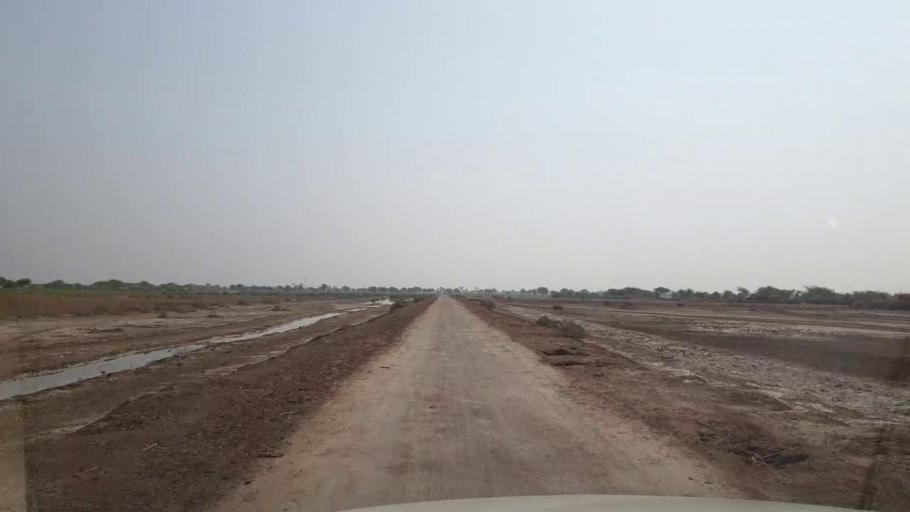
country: PK
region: Sindh
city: Chor
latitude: 25.4893
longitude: 69.6995
